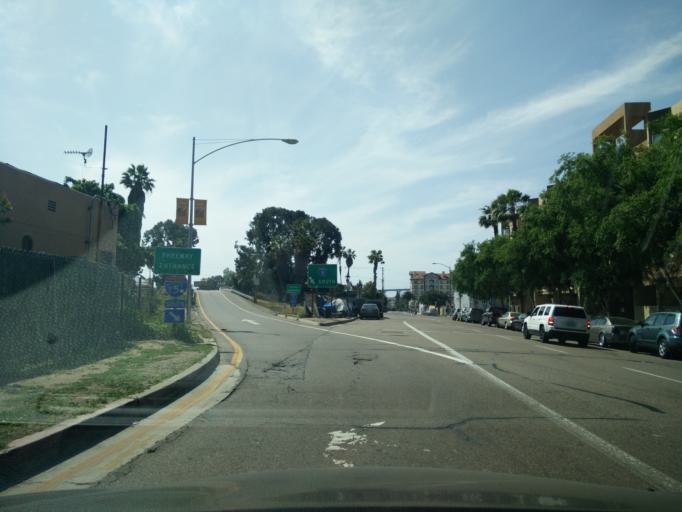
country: US
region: California
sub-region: San Diego County
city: San Diego
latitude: 32.7092
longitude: -117.1485
